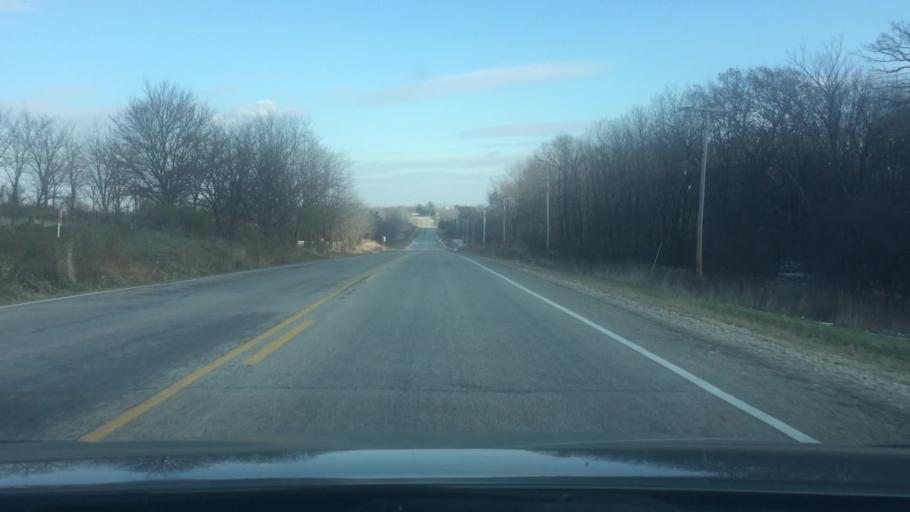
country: US
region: Wisconsin
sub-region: Walworth County
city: Whitewater
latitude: 42.9311
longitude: -88.6961
